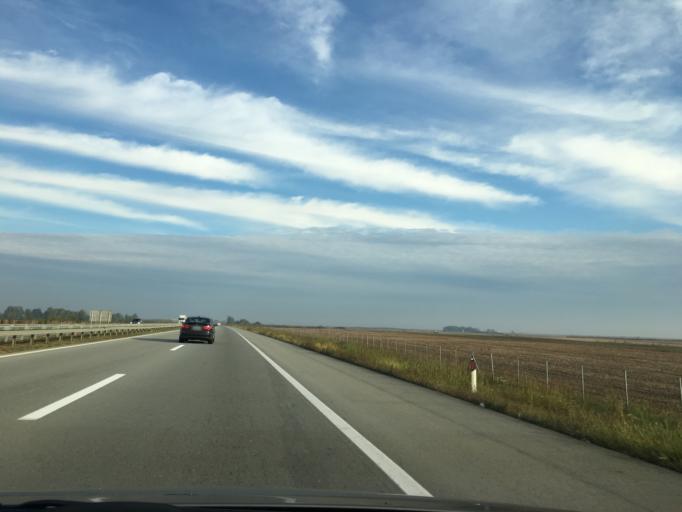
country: RS
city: Gardinovci
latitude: 45.1971
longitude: 20.0742
